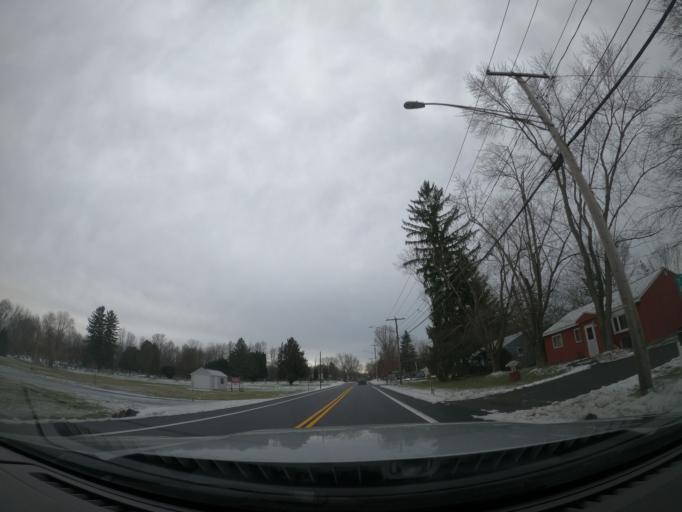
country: US
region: New York
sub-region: Madison County
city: Bridgeport
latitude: 43.1491
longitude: -75.9753
